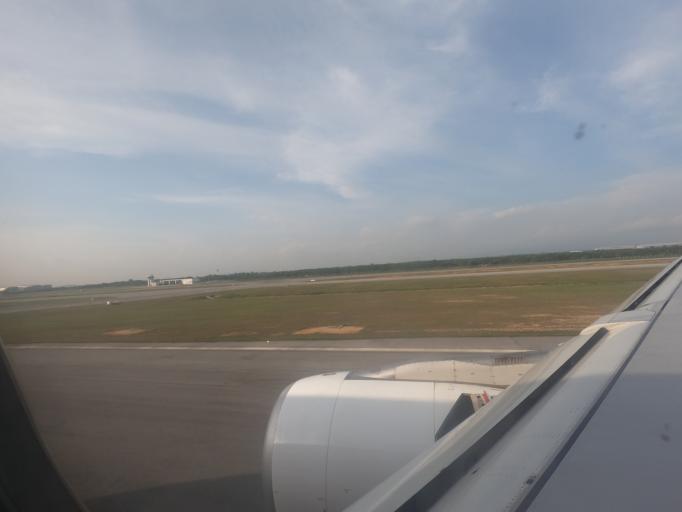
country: MY
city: Sungai Pelek New Village
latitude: 2.7194
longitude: 101.6901
